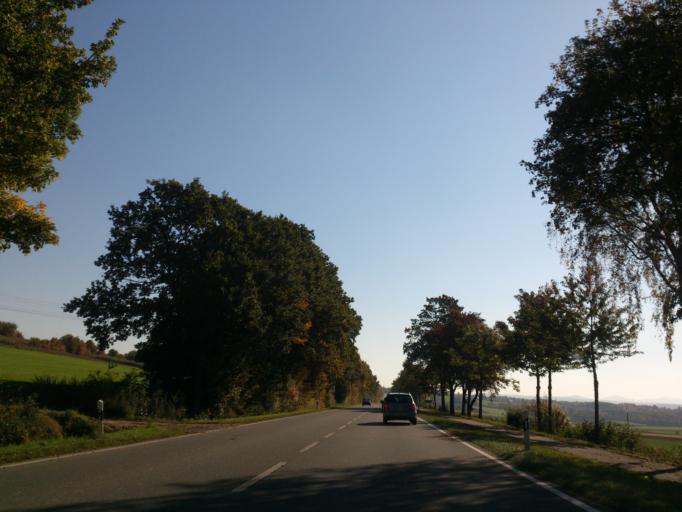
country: DE
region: North Rhine-Westphalia
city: Warburg
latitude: 51.5039
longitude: 9.1035
